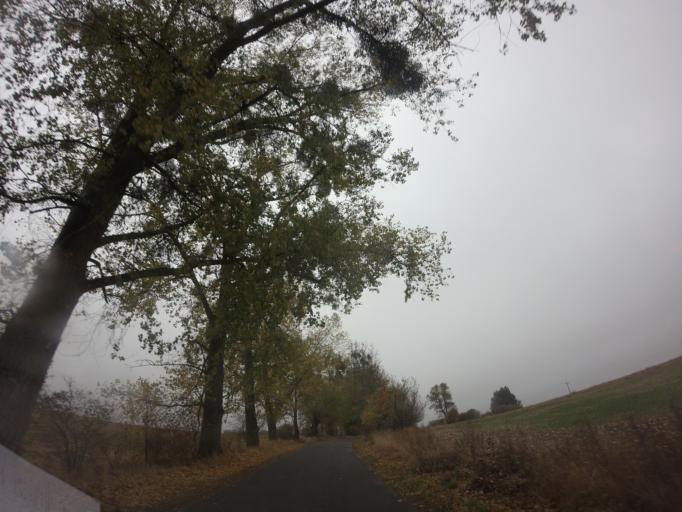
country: PL
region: West Pomeranian Voivodeship
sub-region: Powiat choszczenski
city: Choszczno
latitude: 53.1198
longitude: 15.3983
